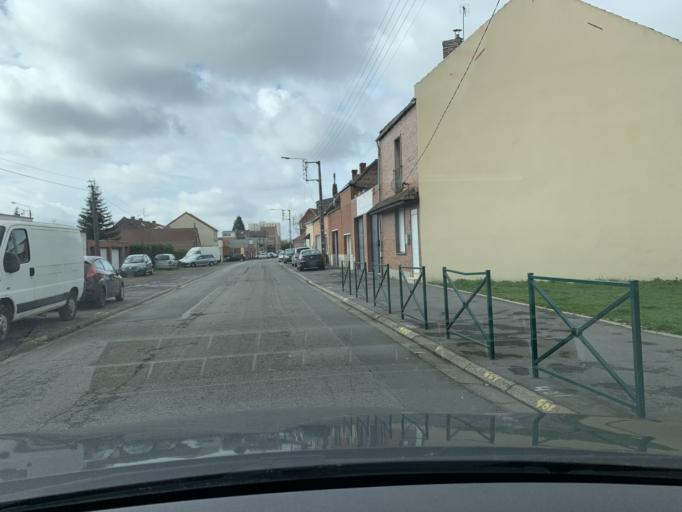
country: FR
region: Nord-Pas-de-Calais
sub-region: Departement du Nord
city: Roost-Warendin
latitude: 50.3978
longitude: 3.0887
